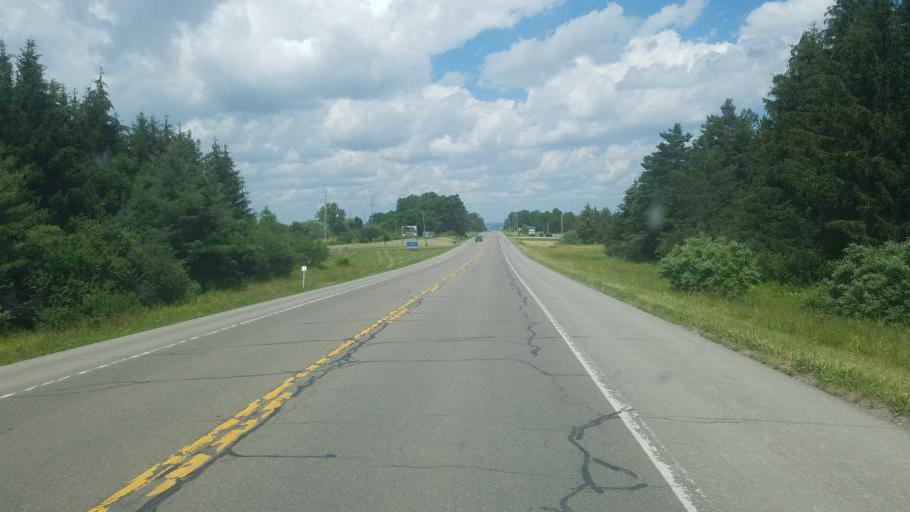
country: US
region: New York
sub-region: Yates County
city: Keuka Park
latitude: 42.5826
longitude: -77.0365
